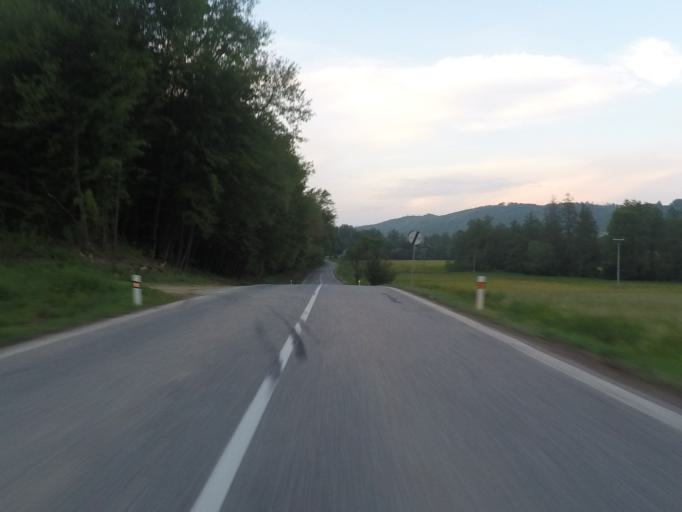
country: SK
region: Banskobystricky
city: Tisovec
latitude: 48.5269
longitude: 19.9482
